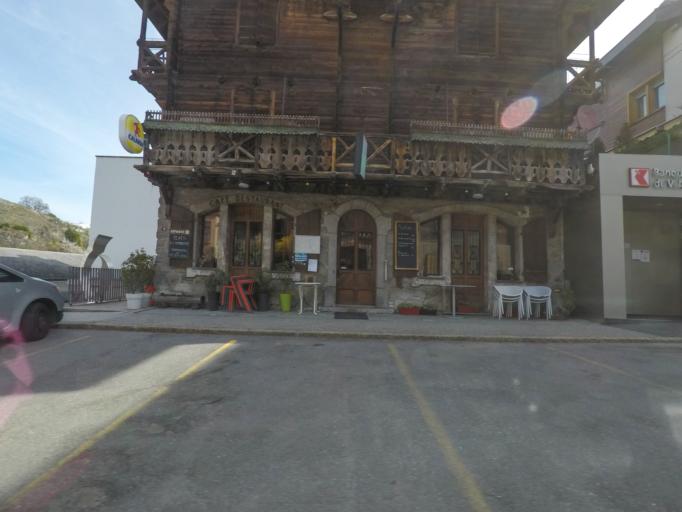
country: CH
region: Valais
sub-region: Herens District
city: Vex
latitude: 46.2120
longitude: 7.3984
